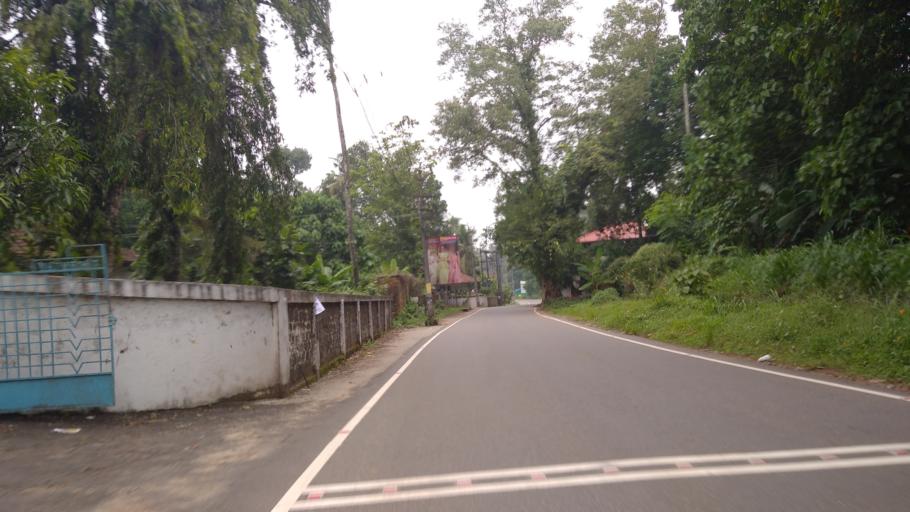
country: IN
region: Kerala
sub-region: Ernakulam
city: Perumpavur
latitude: 10.1208
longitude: 76.5349
